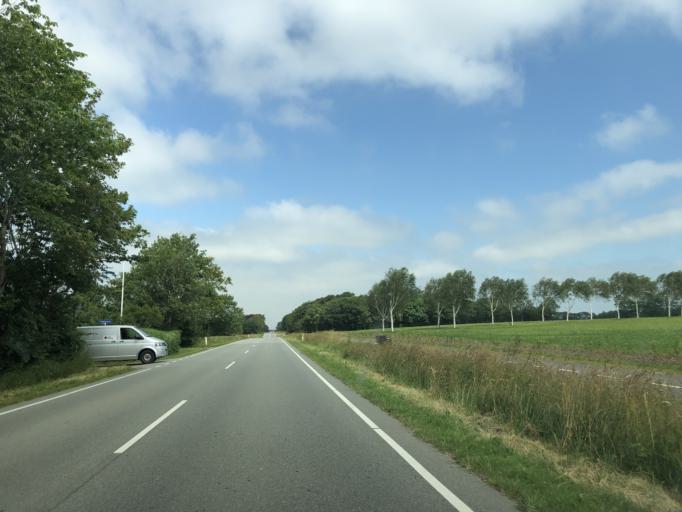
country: DK
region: South Denmark
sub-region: Varde Kommune
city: Varde
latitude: 55.6459
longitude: 8.4873
